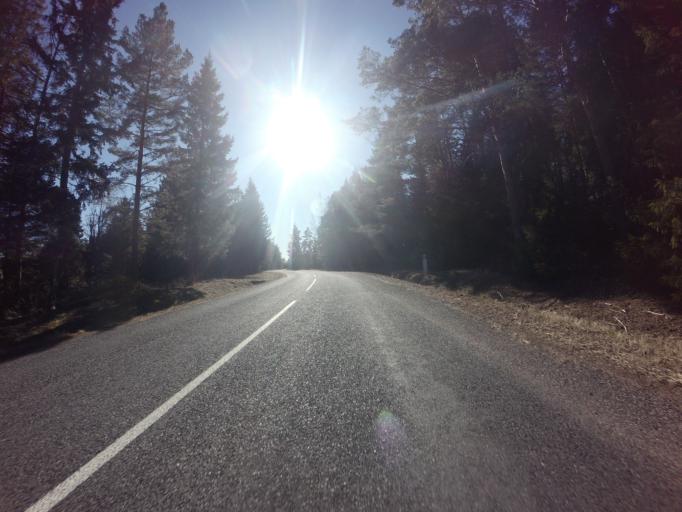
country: EE
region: Saare
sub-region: Kuressaare linn
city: Kuressaare
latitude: 58.5826
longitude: 22.5593
